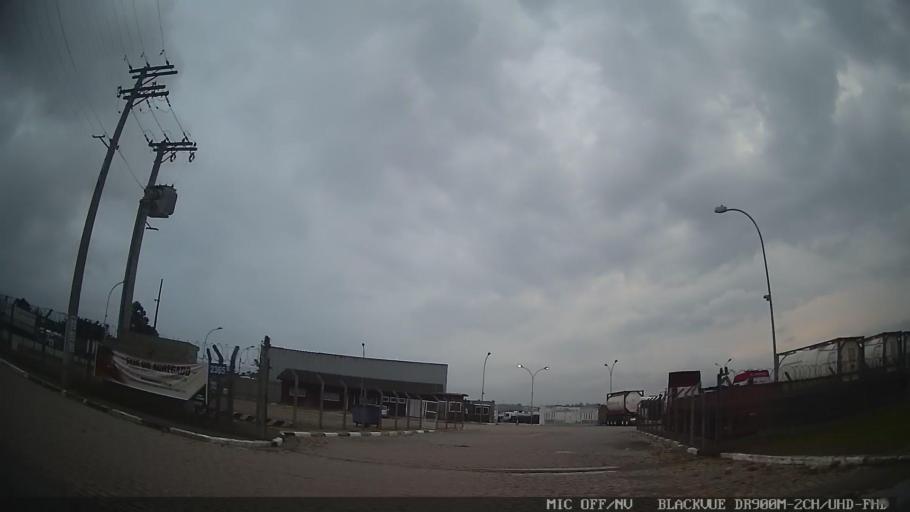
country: BR
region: Sao Paulo
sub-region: Suzano
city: Suzano
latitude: -23.5344
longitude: -46.2849
